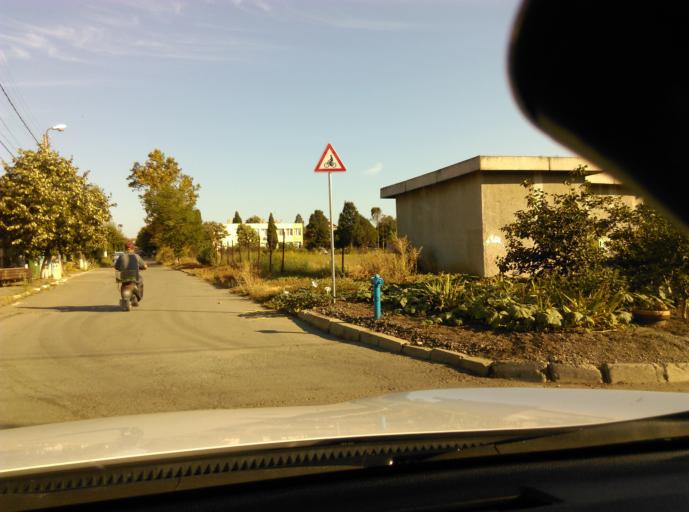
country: BG
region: Burgas
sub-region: Obshtina Kameno
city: Kameno
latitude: 42.5993
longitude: 27.3846
